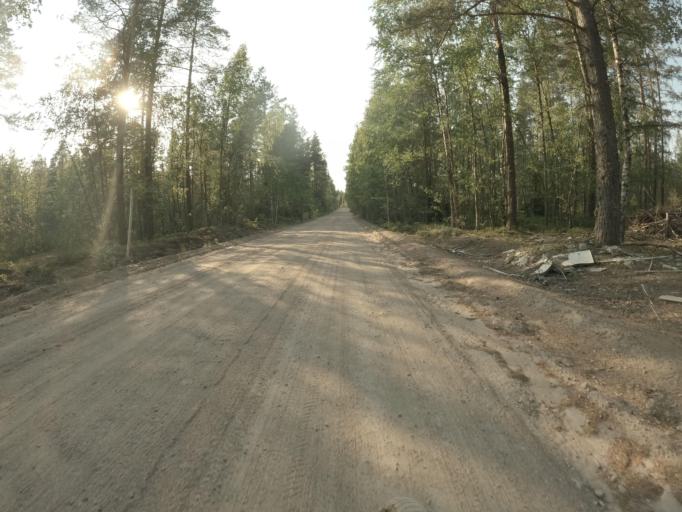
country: RU
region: Leningrad
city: Veshchevo
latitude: 60.4600
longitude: 29.2442
